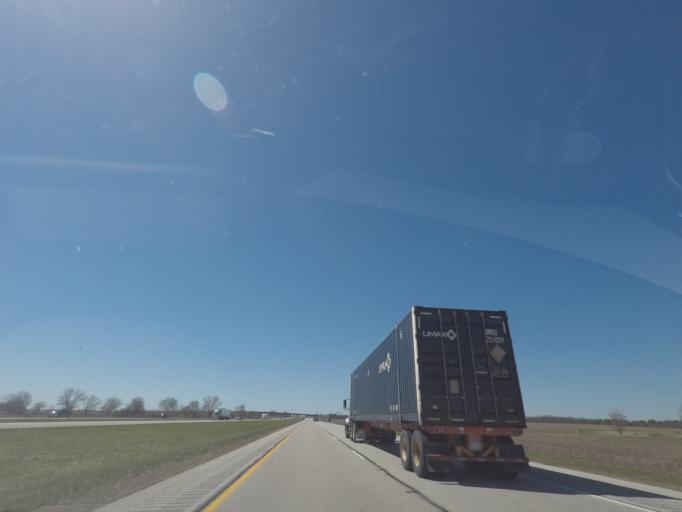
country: US
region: Illinois
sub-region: McLean County
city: Lexington
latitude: 40.6094
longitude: -88.8330
